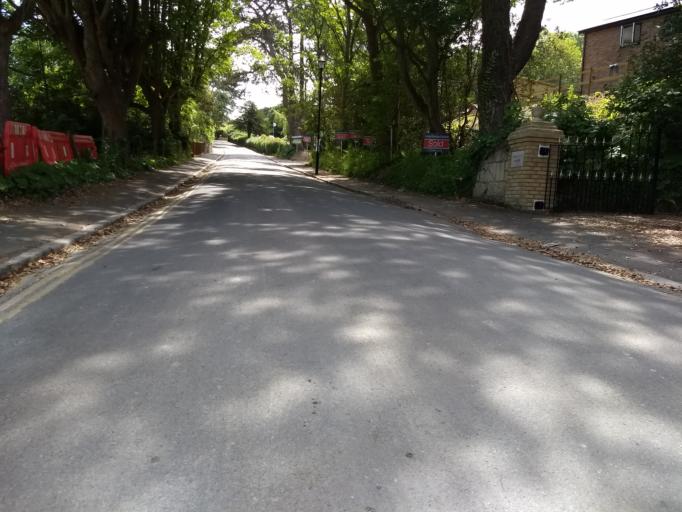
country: GB
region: England
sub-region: Isle of Wight
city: Shanklin
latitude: 50.6219
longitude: -1.1773
